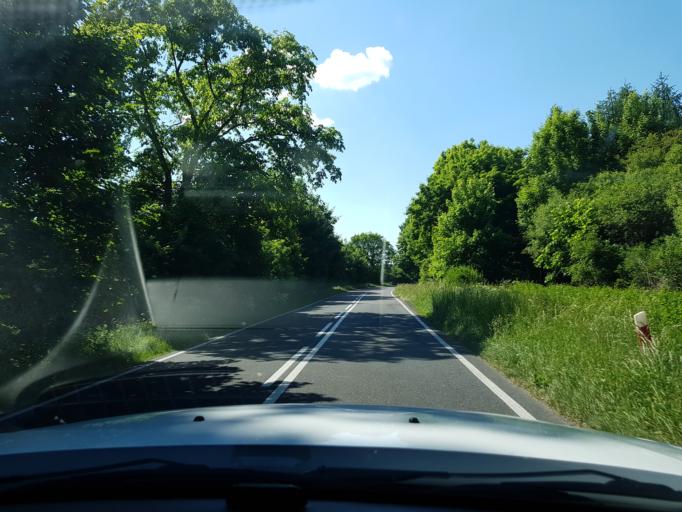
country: PL
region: West Pomeranian Voivodeship
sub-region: Powiat gryfinski
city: Gryfino
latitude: 53.1834
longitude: 14.5408
